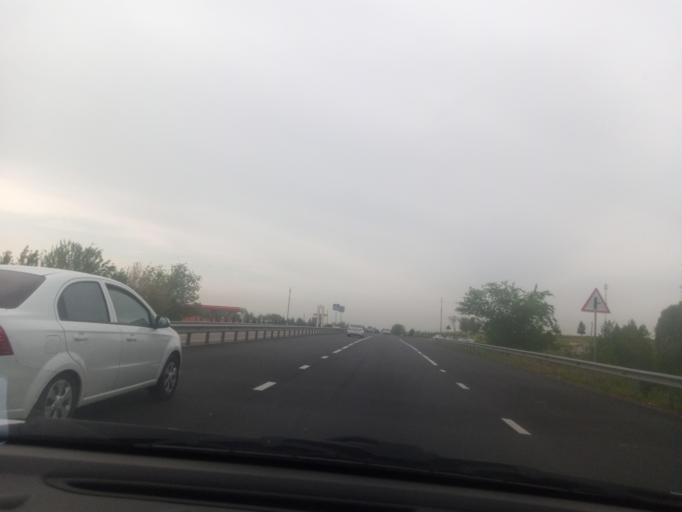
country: UZ
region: Toshkent
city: Tuytepa
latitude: 41.1242
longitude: 69.4391
